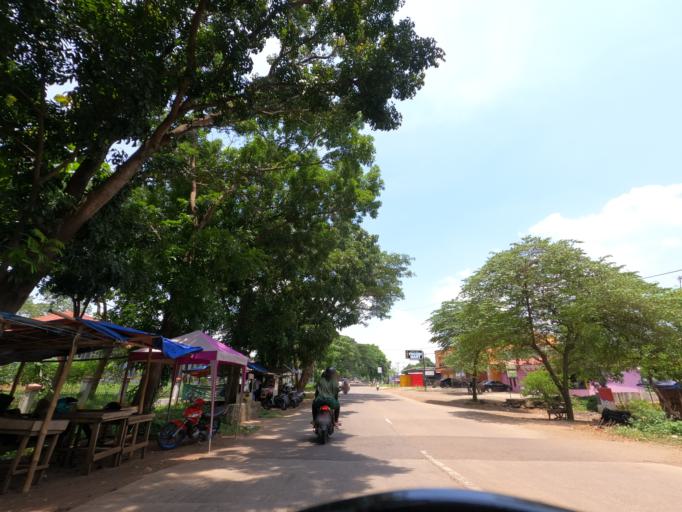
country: ID
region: West Java
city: Pamanukan
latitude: -6.5494
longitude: 107.7652
